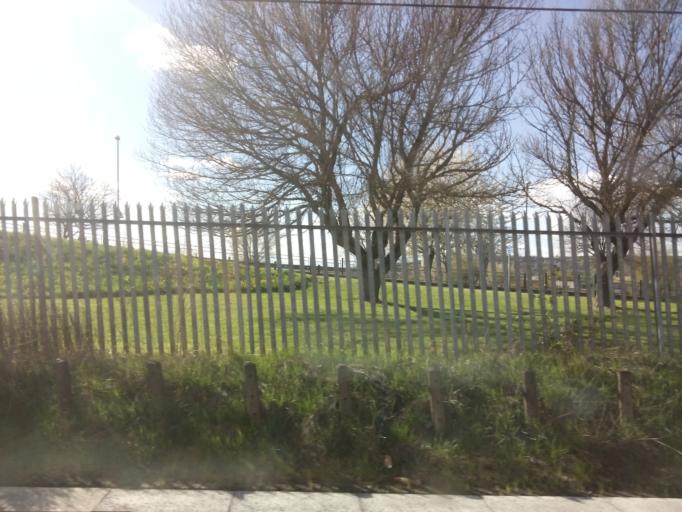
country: GB
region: England
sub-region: Newcastle upon Tyne
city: Newcastle upon Tyne
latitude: 54.9583
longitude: -1.6175
